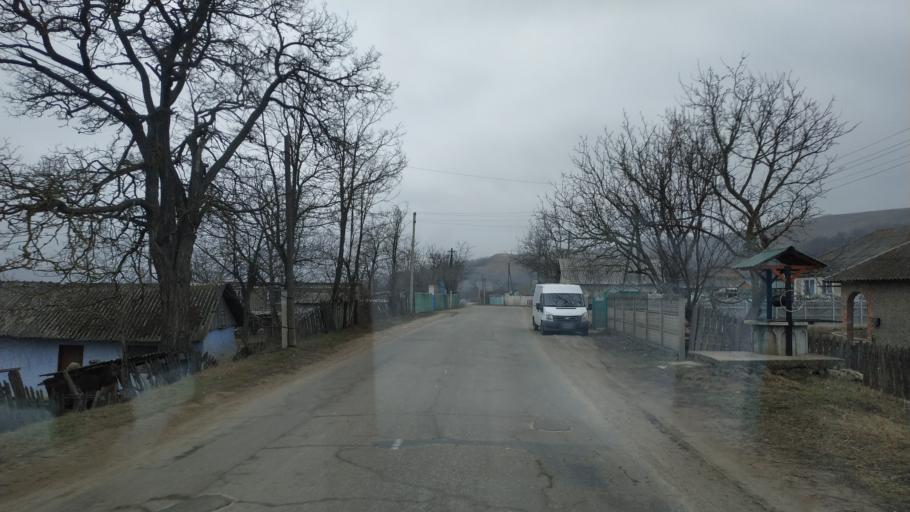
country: MD
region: Hincesti
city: Hincesti
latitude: 46.9826
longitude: 28.4506
